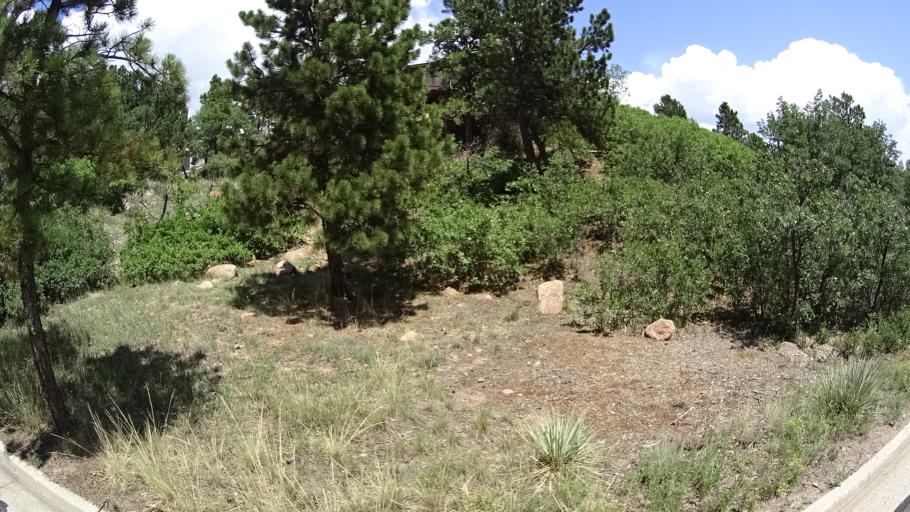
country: US
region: Colorado
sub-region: El Paso County
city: Air Force Academy
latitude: 38.9331
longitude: -104.8245
